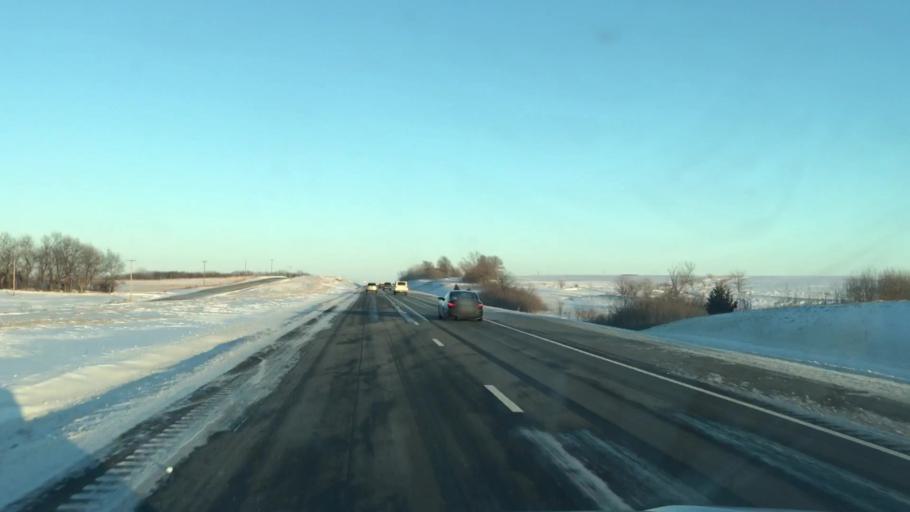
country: US
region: Missouri
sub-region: Clinton County
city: Gower
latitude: 39.7619
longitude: -94.5338
